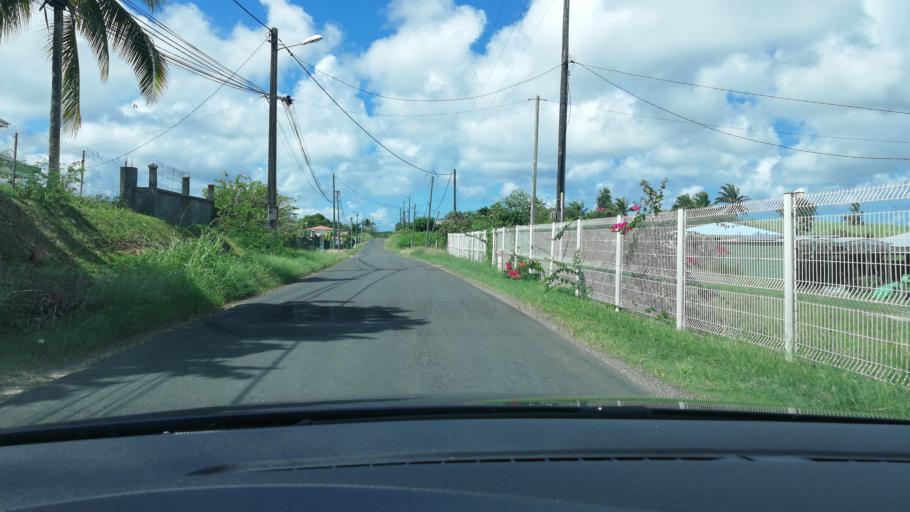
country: GP
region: Guadeloupe
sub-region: Guadeloupe
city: Petit-Canal
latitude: 16.3794
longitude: -61.4420
